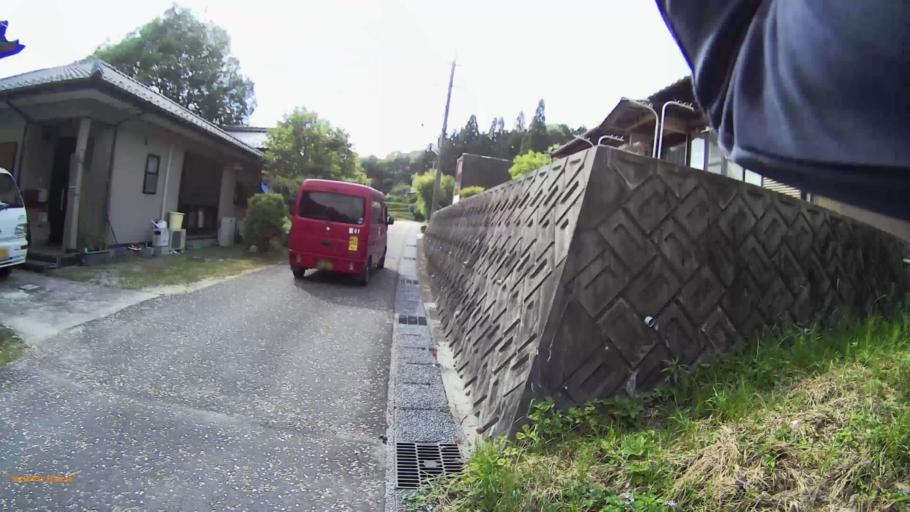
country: JP
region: Gifu
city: Mizunami
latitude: 35.4462
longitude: 137.3590
